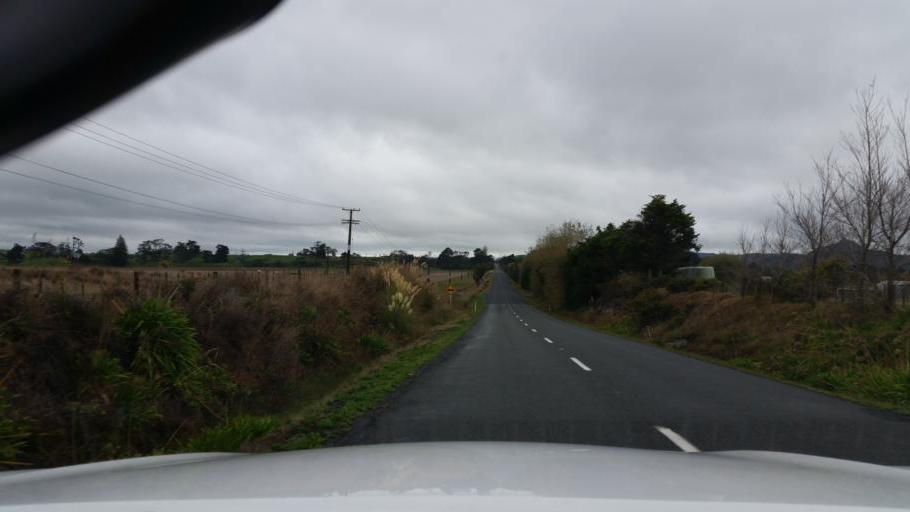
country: NZ
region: Northland
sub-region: Kaipara District
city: Dargaville
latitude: -36.0927
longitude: 173.9525
